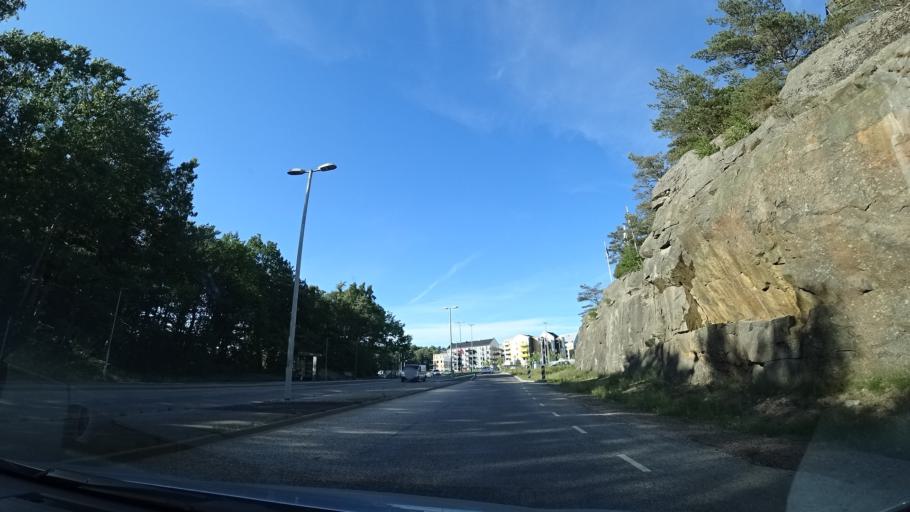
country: SE
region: Vaestra Goetaland
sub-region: Goteborg
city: Billdal
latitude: 57.5974
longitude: 11.9487
